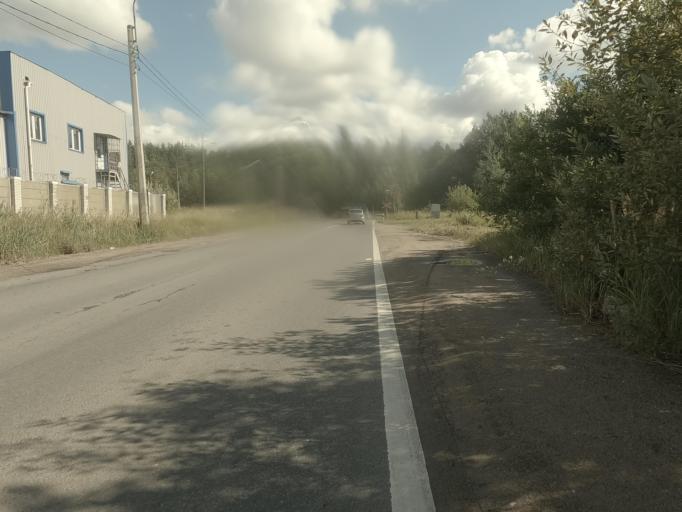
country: RU
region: St.-Petersburg
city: Krasnogvargeisky
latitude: 59.9738
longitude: 30.5274
